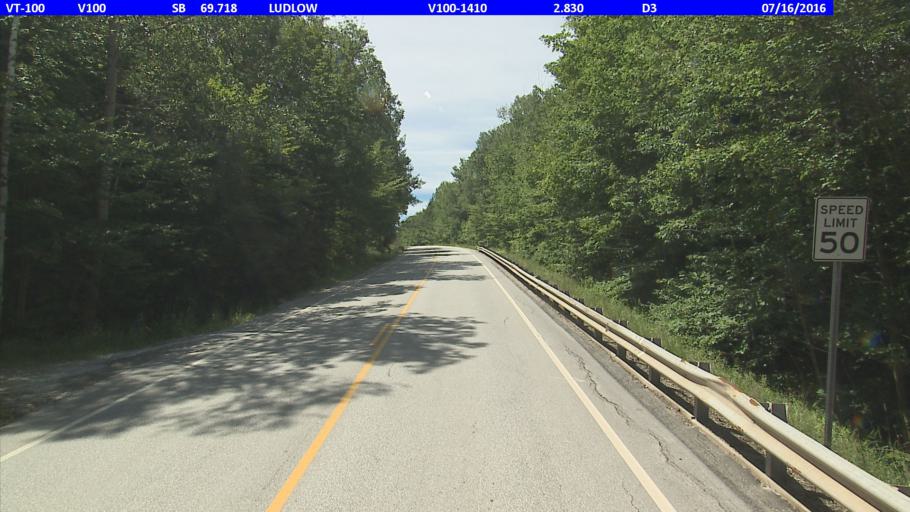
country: US
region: Vermont
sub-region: Windsor County
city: Chester
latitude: 43.3683
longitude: -72.7199
